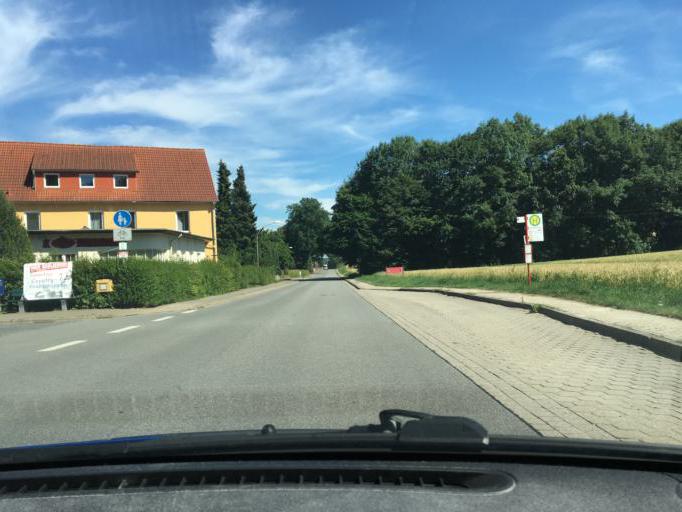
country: DE
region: Lower Saxony
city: Bendestorf
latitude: 53.3413
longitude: 9.9619
